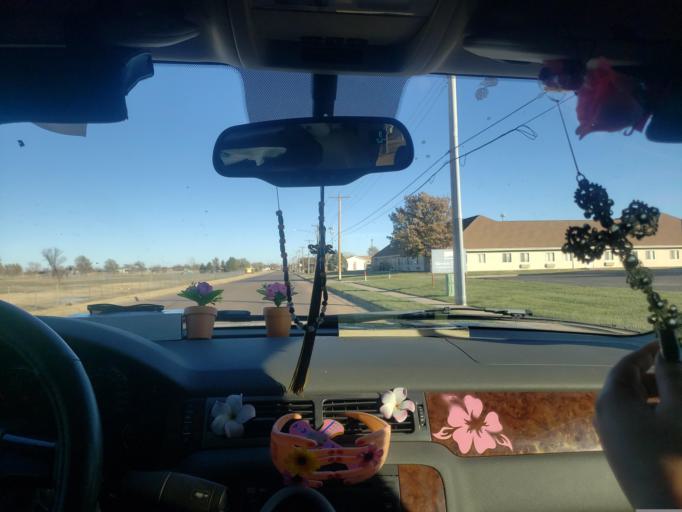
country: US
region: Kansas
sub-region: Finney County
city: Garden City
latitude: 37.9676
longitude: -100.8458
